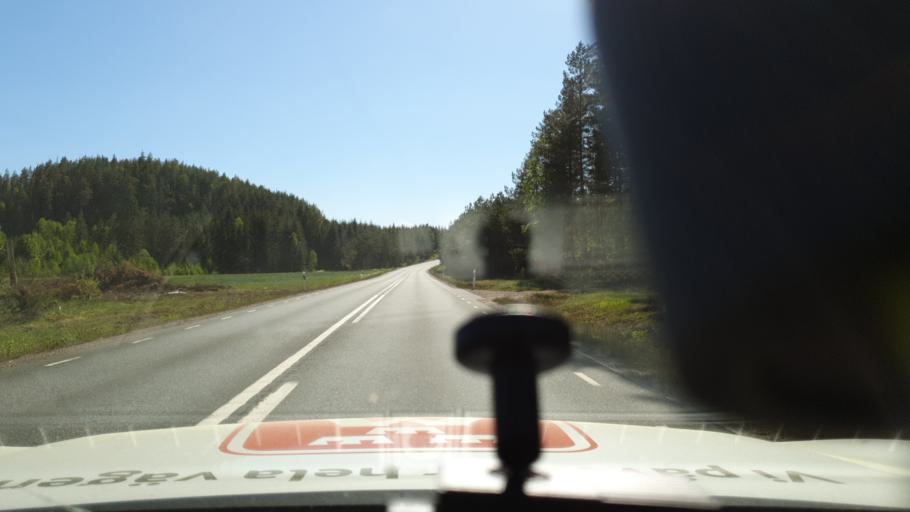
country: SE
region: Kalmar
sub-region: Hultsfreds Kommun
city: Virserum
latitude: 57.3987
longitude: 15.4591
